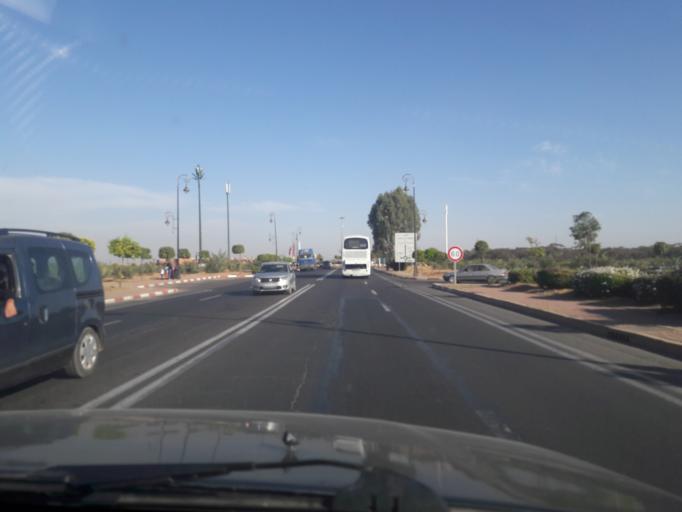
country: MA
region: Marrakech-Tensift-Al Haouz
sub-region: Marrakech
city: Marrakesh
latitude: 31.6479
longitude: -7.9316
